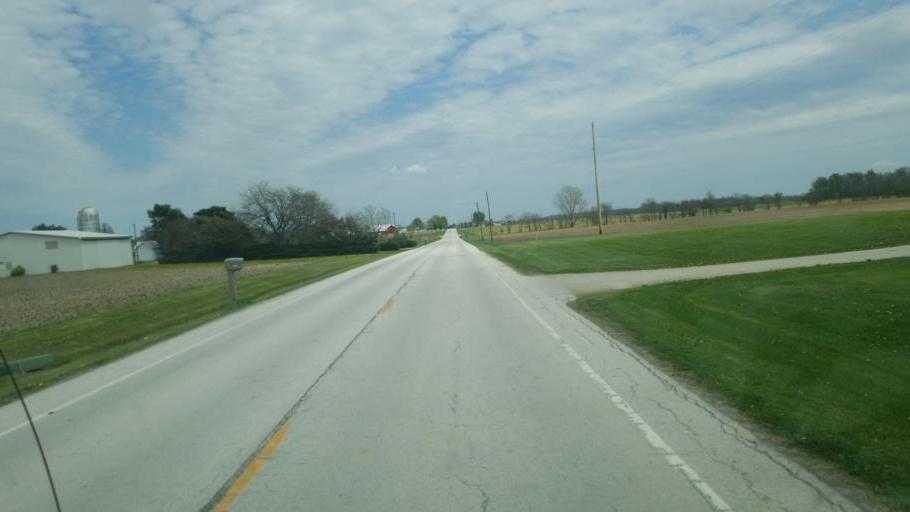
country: US
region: Ohio
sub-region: Hardin County
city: Forest
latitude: 40.8325
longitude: -83.4757
